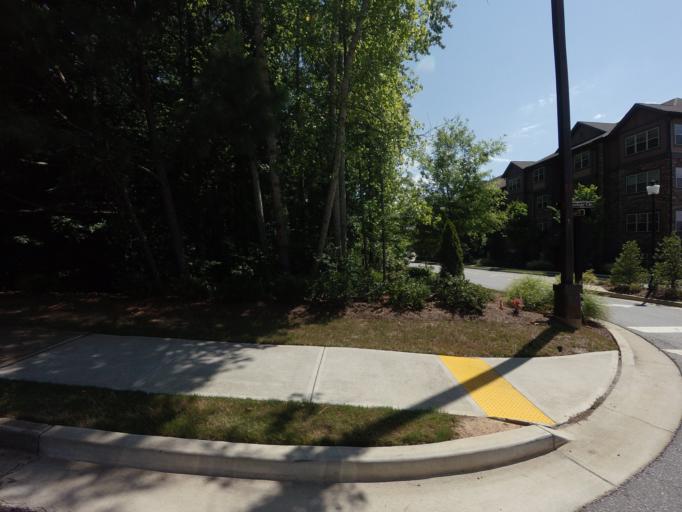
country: US
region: Georgia
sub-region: Fulton County
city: Johns Creek
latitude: 34.0565
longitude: -84.1649
